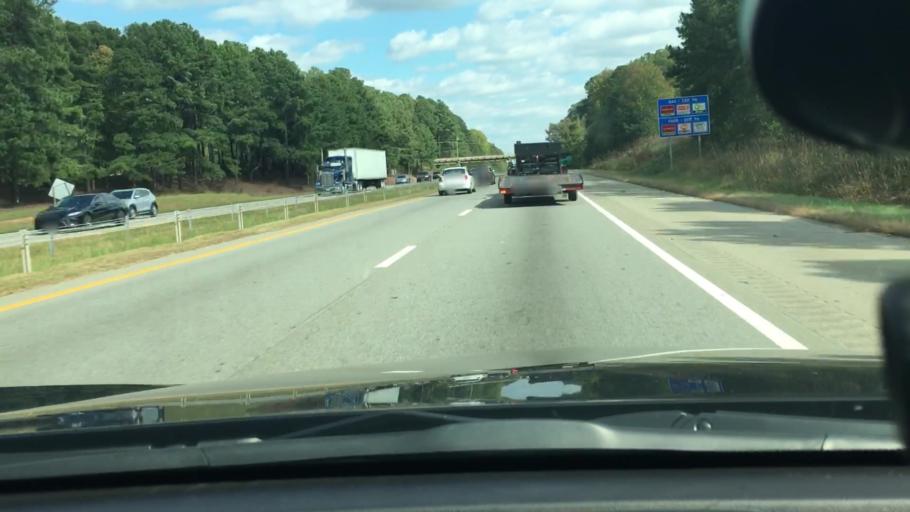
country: US
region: North Carolina
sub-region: Wake County
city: Apex
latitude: 35.7227
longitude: -78.8264
